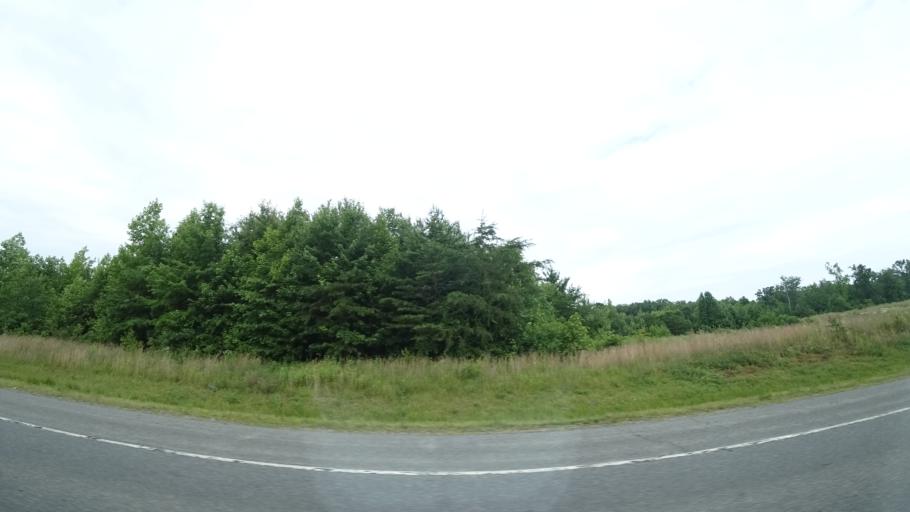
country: US
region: Virginia
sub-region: Spotsylvania County
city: Spotsylvania Courthouse
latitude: 38.1684
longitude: -77.6365
